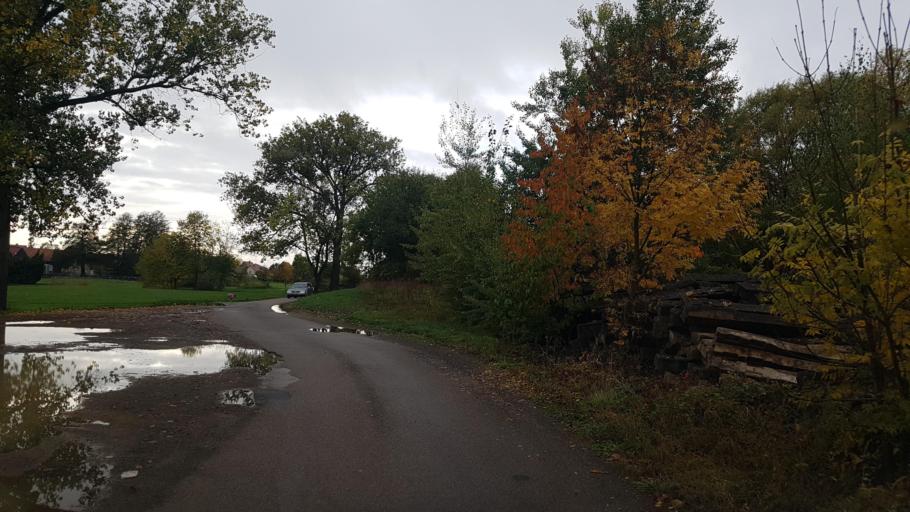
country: DE
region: Brandenburg
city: Schlieben
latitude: 51.7288
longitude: 13.3784
